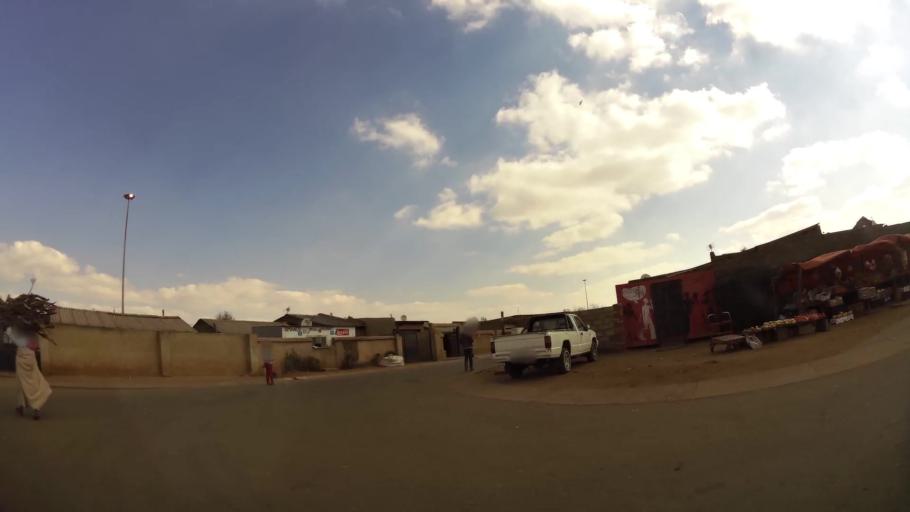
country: ZA
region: Gauteng
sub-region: Ekurhuleni Metropolitan Municipality
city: Tembisa
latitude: -25.9953
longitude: 28.2356
